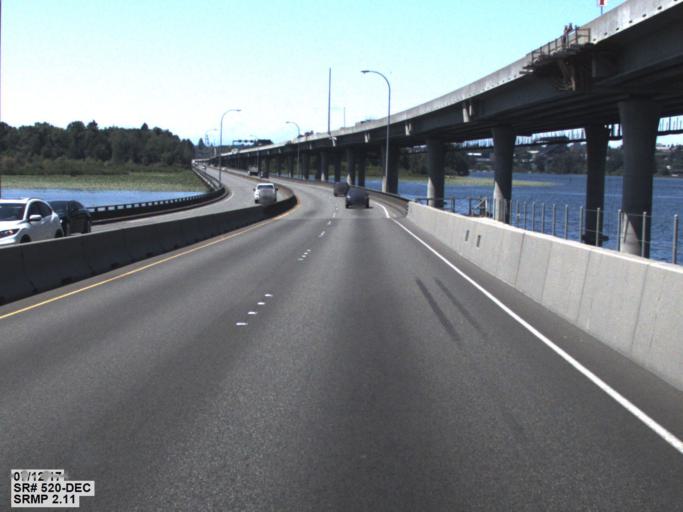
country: US
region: Washington
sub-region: King County
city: Medina
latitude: 47.6443
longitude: -122.2795
